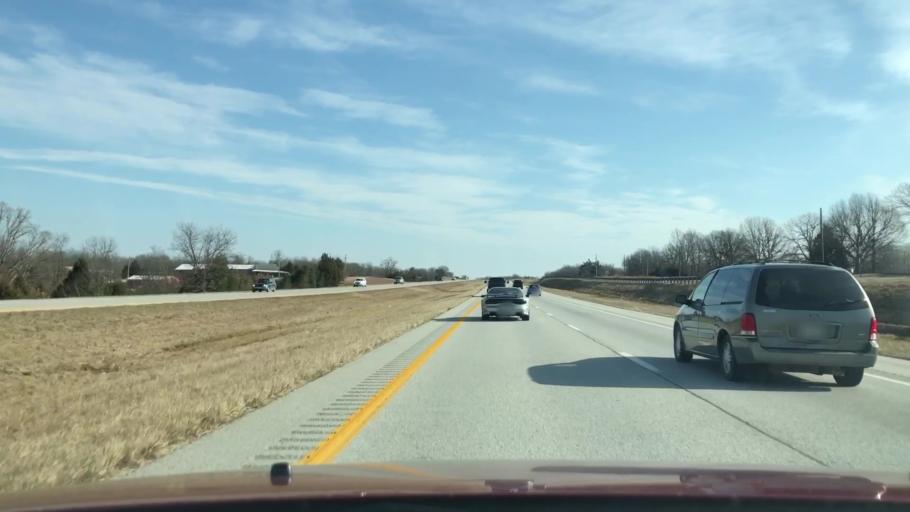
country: US
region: Missouri
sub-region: Webster County
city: Seymour
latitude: 37.1598
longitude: -92.9113
